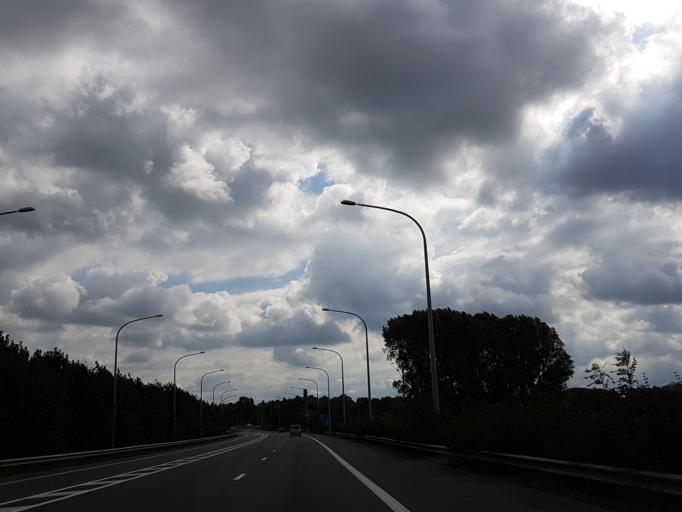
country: BE
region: Flanders
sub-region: Provincie Vlaams-Brabant
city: Tienen
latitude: 50.7972
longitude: 4.9249
